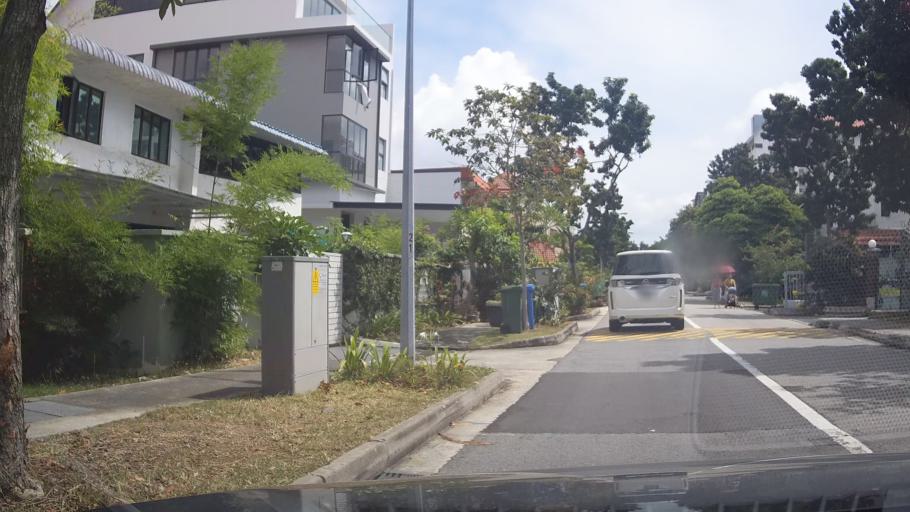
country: SG
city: Singapore
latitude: 1.3149
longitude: 103.9033
